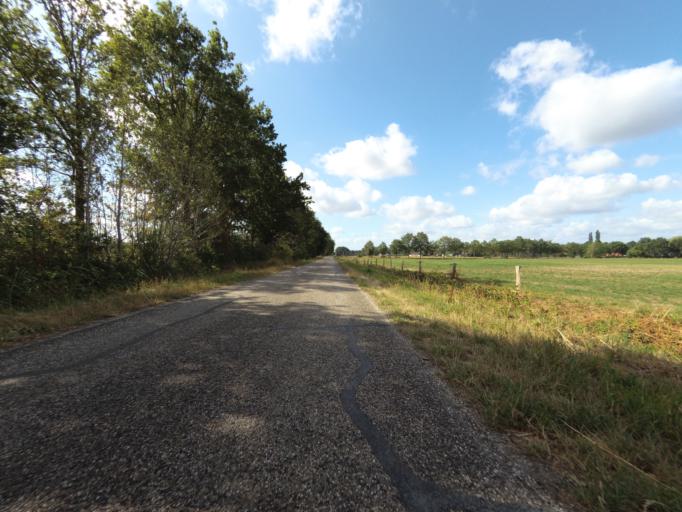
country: NL
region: Overijssel
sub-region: Gemeente Haaksbergen
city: Haaksbergen
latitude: 52.1332
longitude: 6.7612
